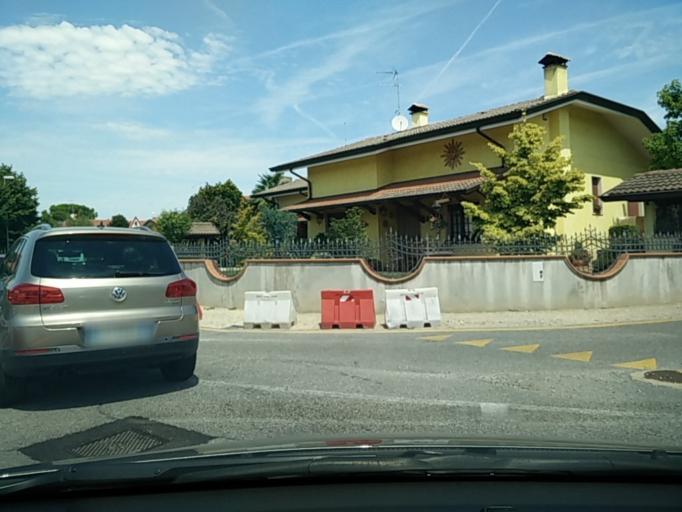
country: IT
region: Veneto
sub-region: Provincia di Venezia
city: Iesolo
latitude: 45.5598
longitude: 12.6410
